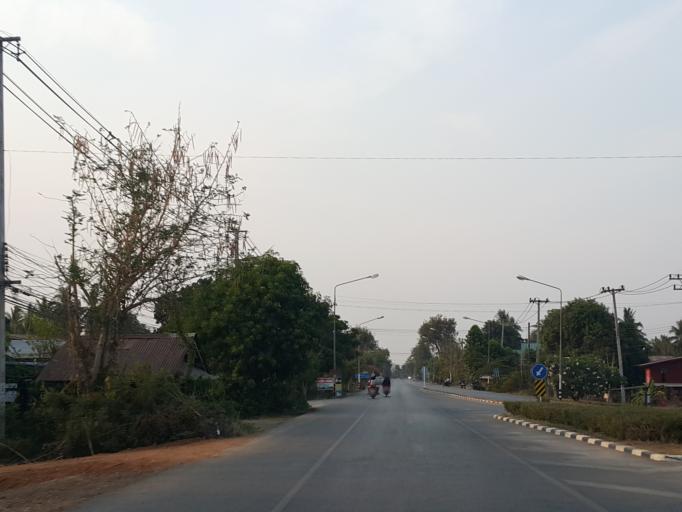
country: TH
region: Sukhothai
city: Sawankhalok
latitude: 17.2788
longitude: 99.8441
